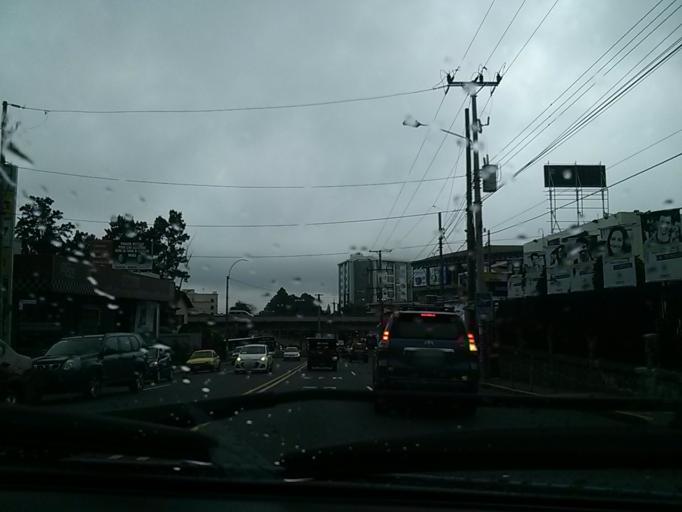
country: CR
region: San Jose
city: San Pedro
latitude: 9.9331
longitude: -84.0548
